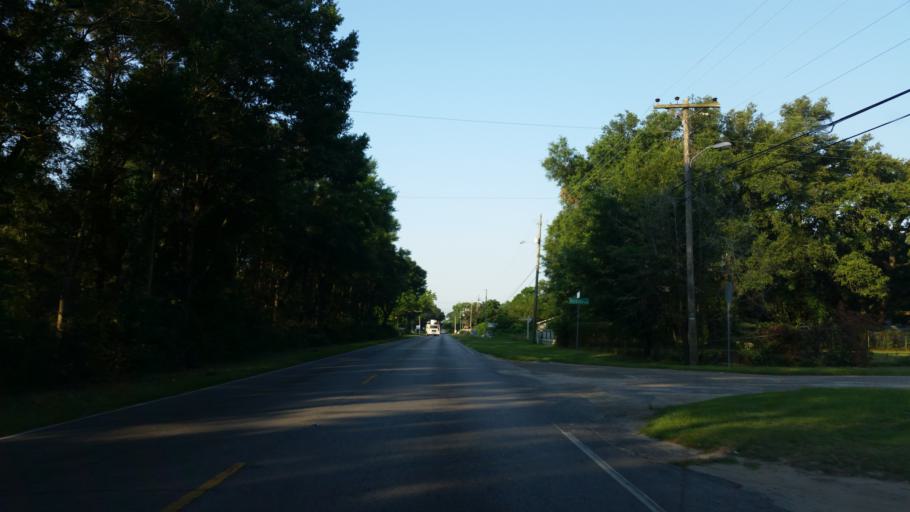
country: US
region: Florida
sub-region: Escambia County
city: West Pensacola
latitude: 30.4215
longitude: -87.2711
